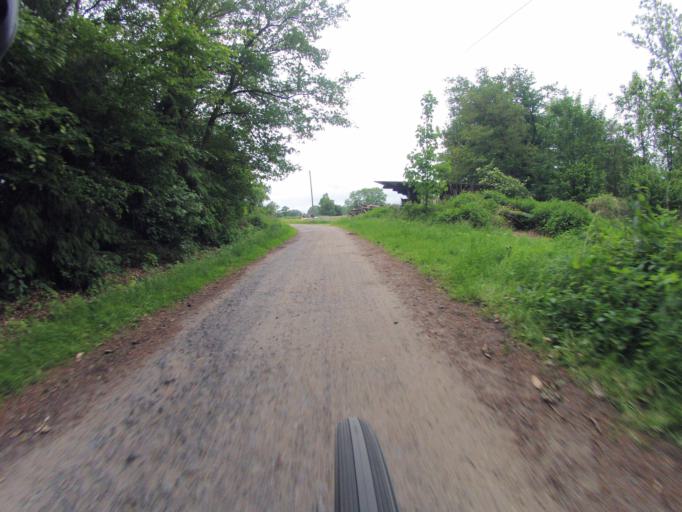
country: DE
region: North Rhine-Westphalia
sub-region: Regierungsbezirk Munster
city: Saerbeck
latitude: 52.1668
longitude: 7.5899
